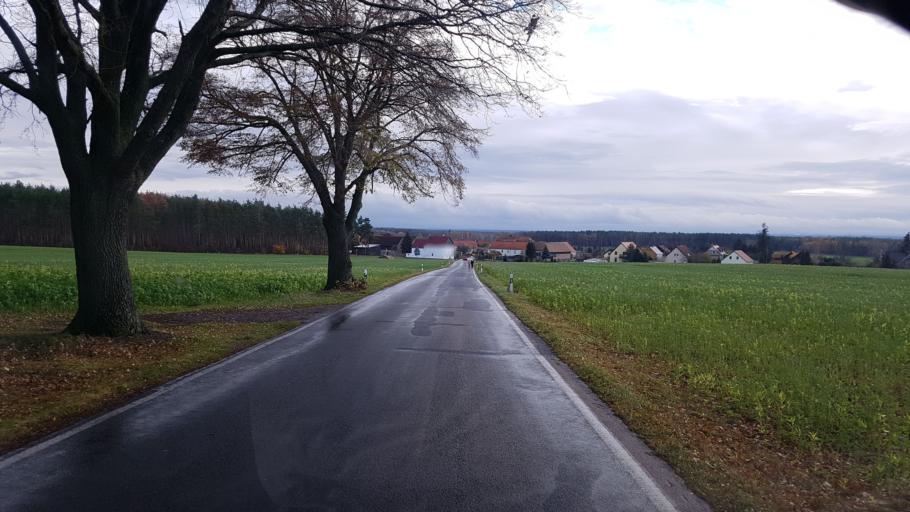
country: DE
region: Saxony
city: Thiendorf
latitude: 51.3238
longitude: 13.7418
